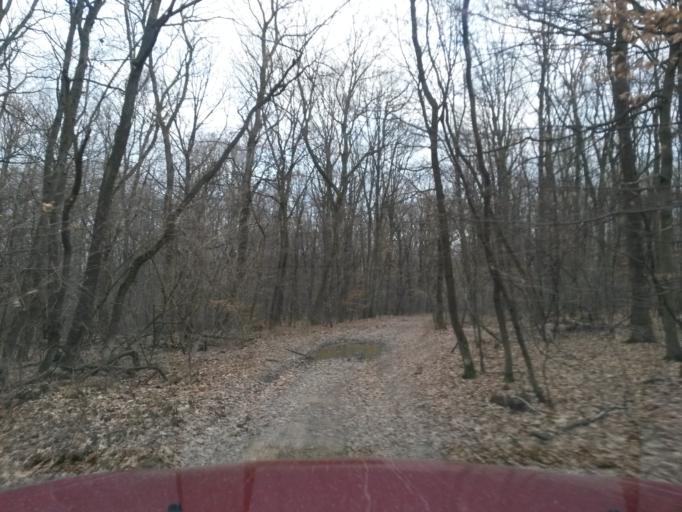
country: SK
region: Kosicky
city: Kosice
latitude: 48.7006
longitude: 21.2969
